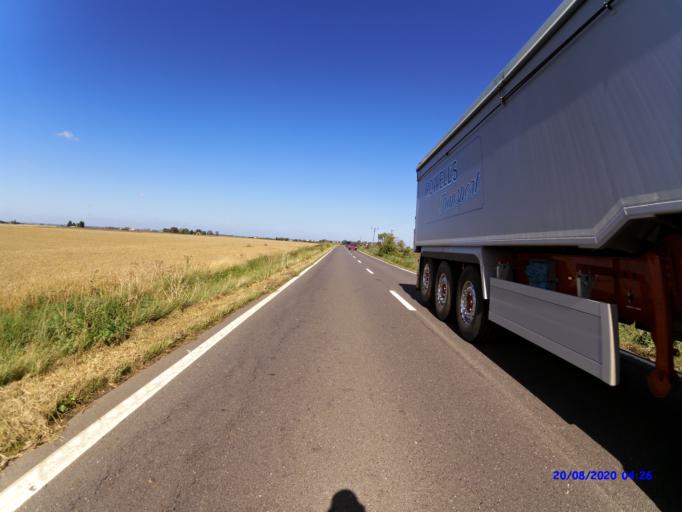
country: GB
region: England
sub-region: Cambridgeshire
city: Whittlesey
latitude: 52.5022
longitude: -0.1314
